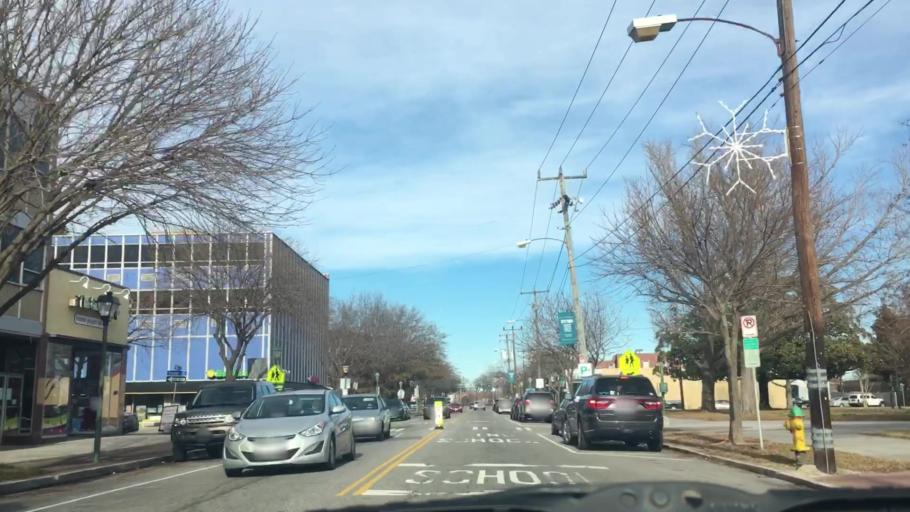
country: US
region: Virginia
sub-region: City of Norfolk
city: Norfolk
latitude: 36.8688
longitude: -76.2974
